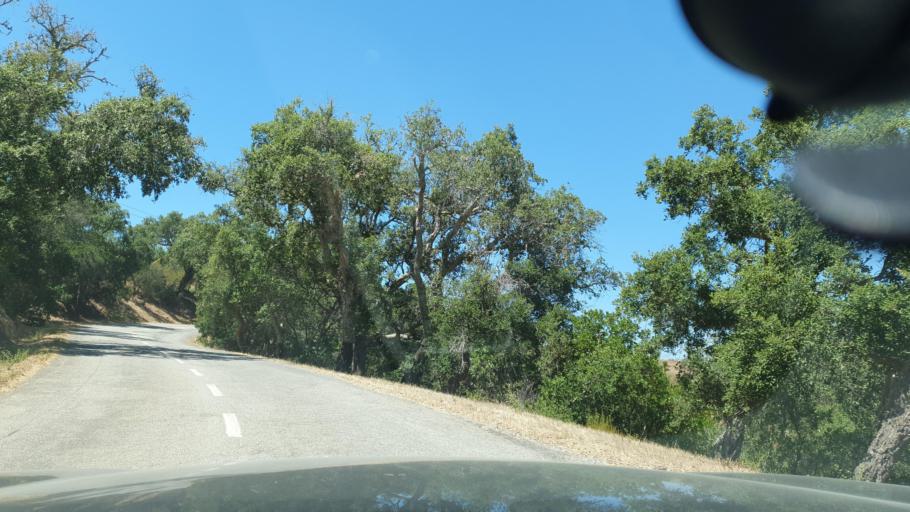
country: PT
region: Beja
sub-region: Odemira
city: Odemira
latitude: 37.6098
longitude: -8.5007
